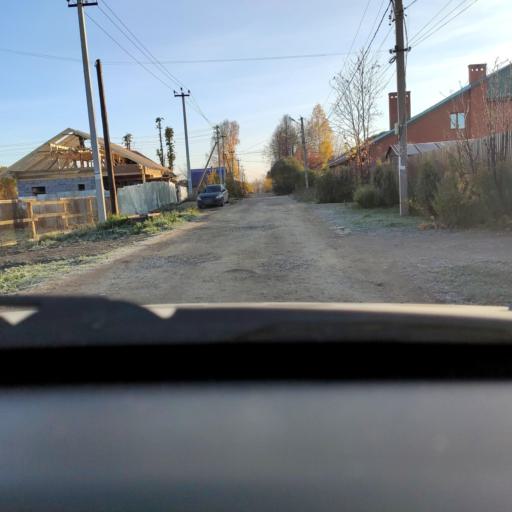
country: RU
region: Perm
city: Perm
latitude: 58.0270
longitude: 56.3266
